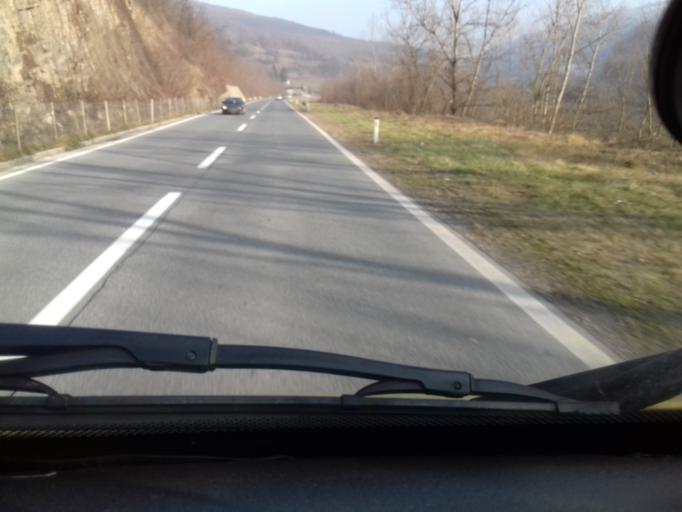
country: BA
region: Federation of Bosnia and Herzegovina
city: Kacuni
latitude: 44.1296
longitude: 17.9616
